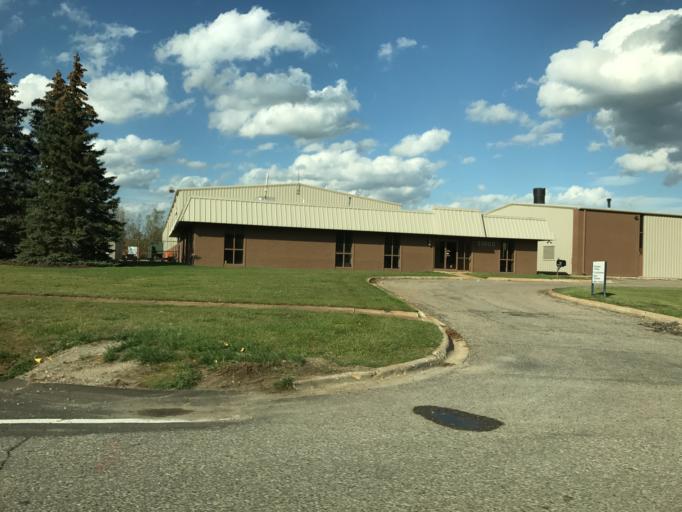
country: US
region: Michigan
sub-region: Oakland County
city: Wixom
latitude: 42.5028
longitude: -83.5746
